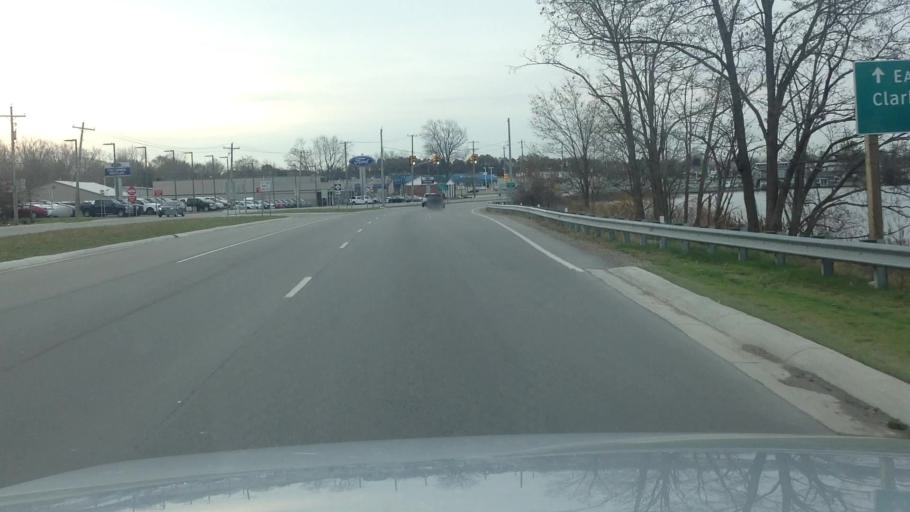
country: US
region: Michigan
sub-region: Oakland County
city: Lake Orion
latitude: 42.7710
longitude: -83.2387
